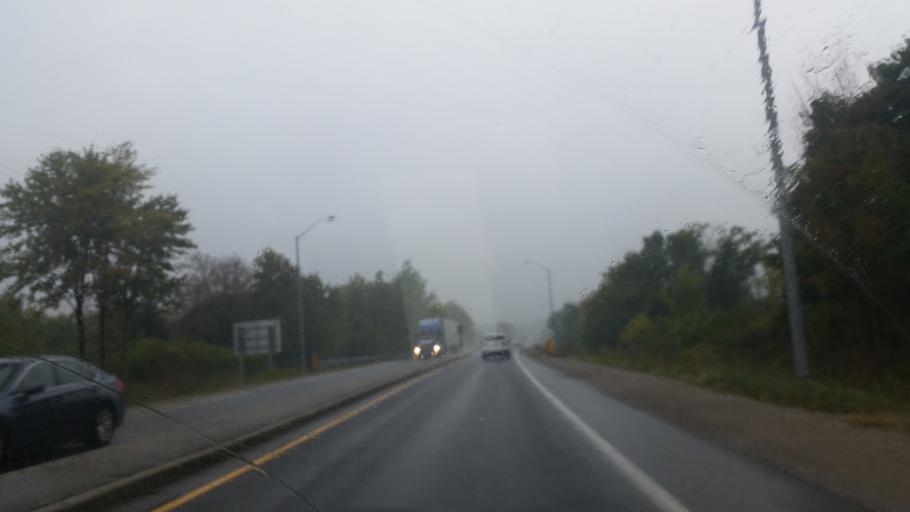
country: CA
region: Ontario
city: Stratford
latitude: 43.2697
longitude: -81.0685
